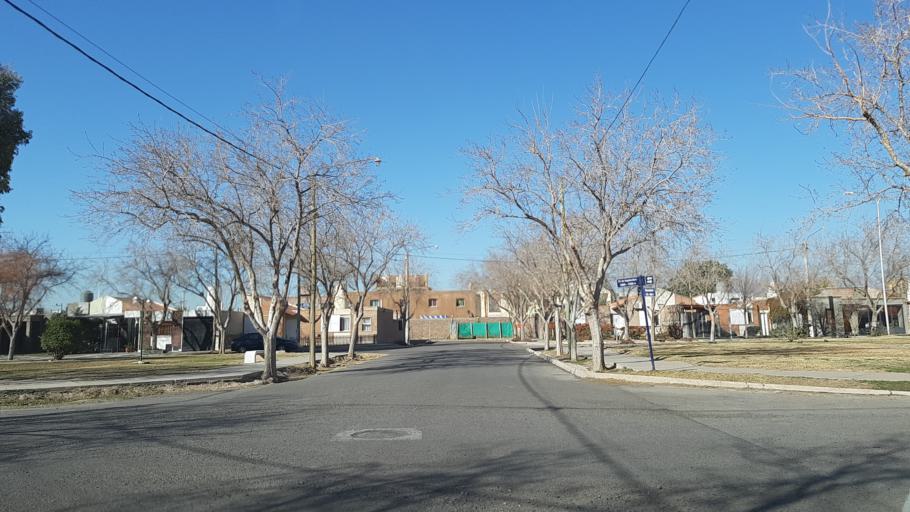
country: AR
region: San Juan
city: San Juan
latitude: -31.5187
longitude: -68.5899
